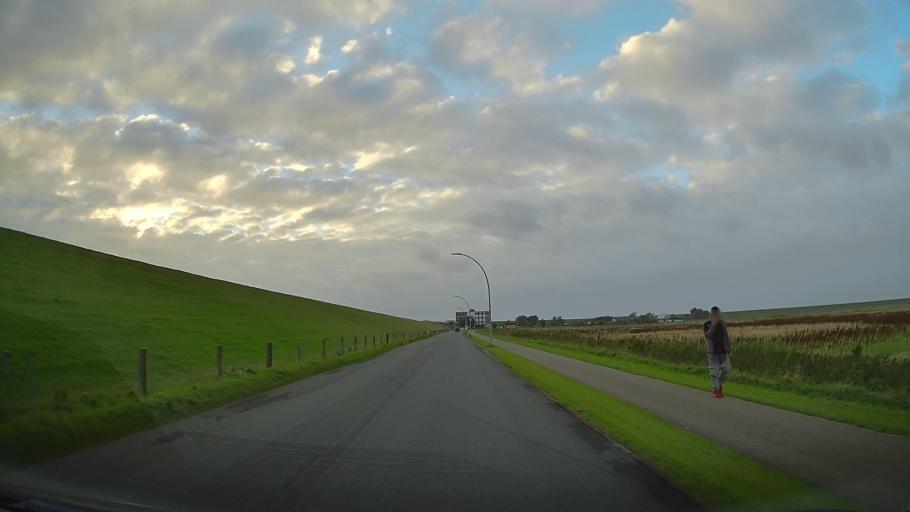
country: DE
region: Schleswig-Holstein
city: Schobull
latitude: 54.4760
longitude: 9.0164
